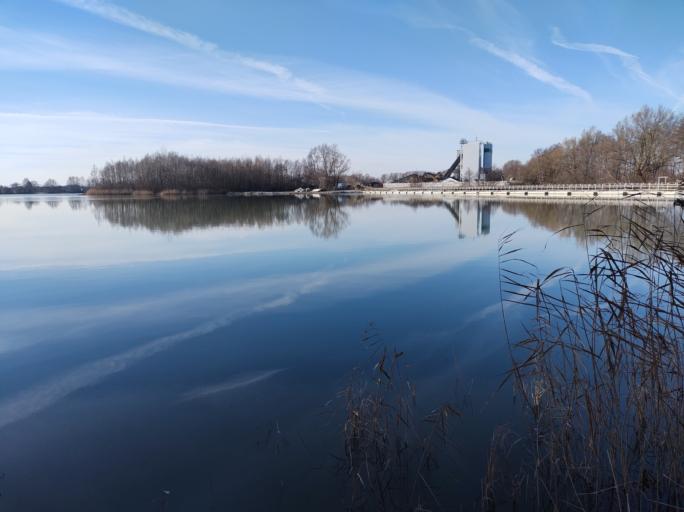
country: DE
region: North Rhine-Westphalia
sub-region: Regierungsbezirk Detmold
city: Hovelhof
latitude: 51.7468
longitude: 8.6399
